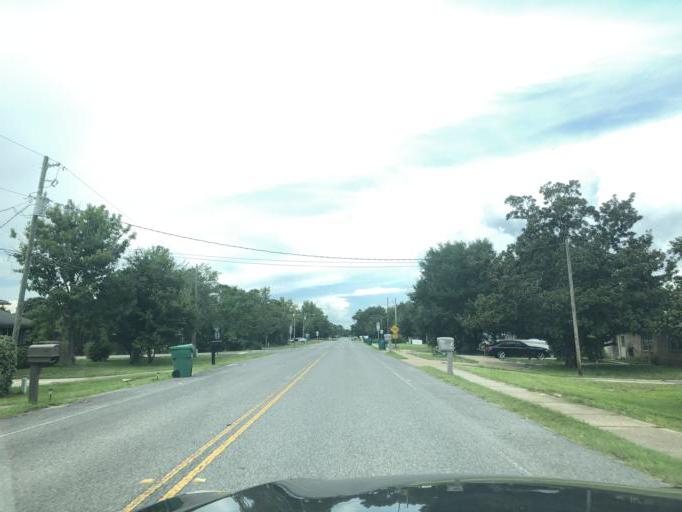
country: US
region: Florida
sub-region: Okaloosa County
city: Destin
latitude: 30.3982
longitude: -86.4952
